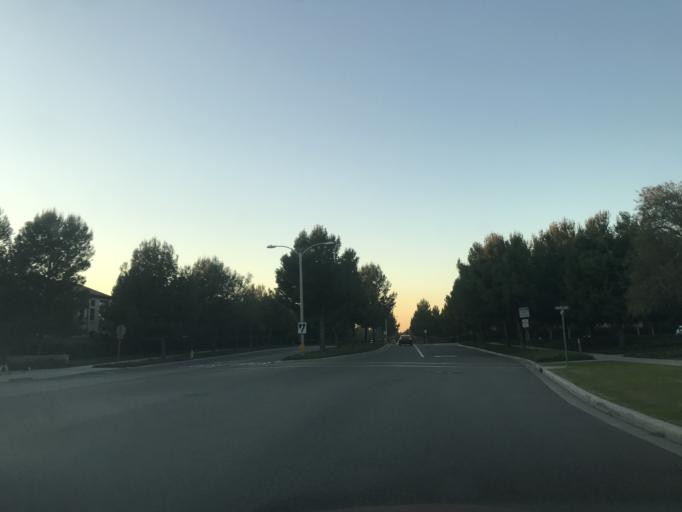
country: US
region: California
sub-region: Orange County
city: Lake Forest
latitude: 33.7056
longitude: -117.7412
